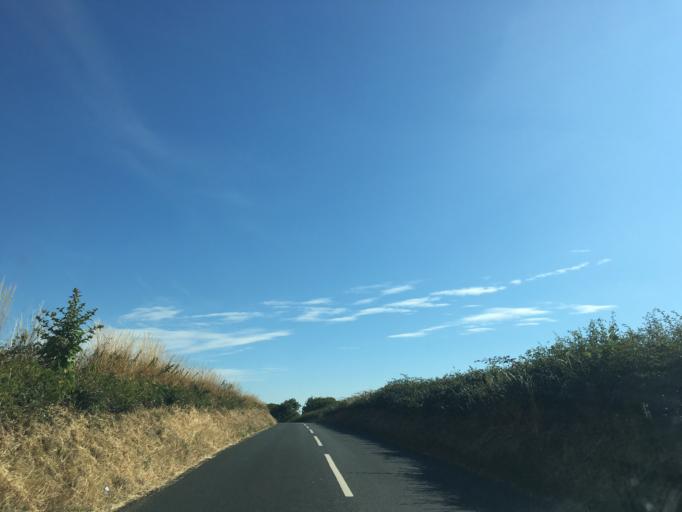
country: GB
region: England
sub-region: Isle of Wight
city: Chale
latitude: 50.6294
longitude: -1.3181
